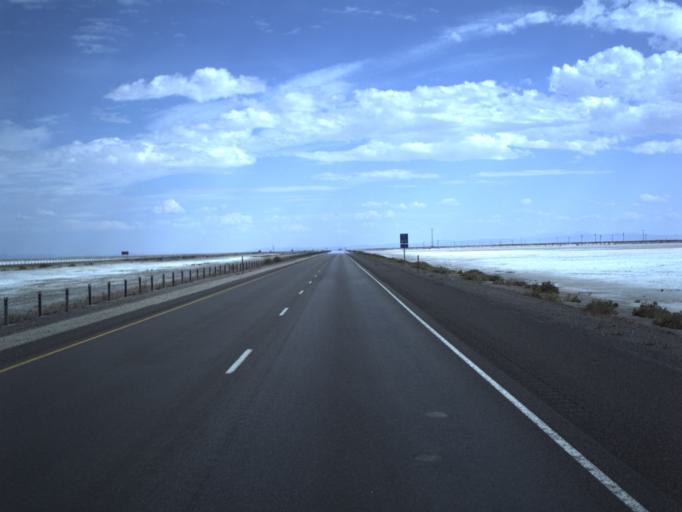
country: US
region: Utah
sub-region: Tooele County
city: Wendover
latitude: 40.7381
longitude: -113.8339
